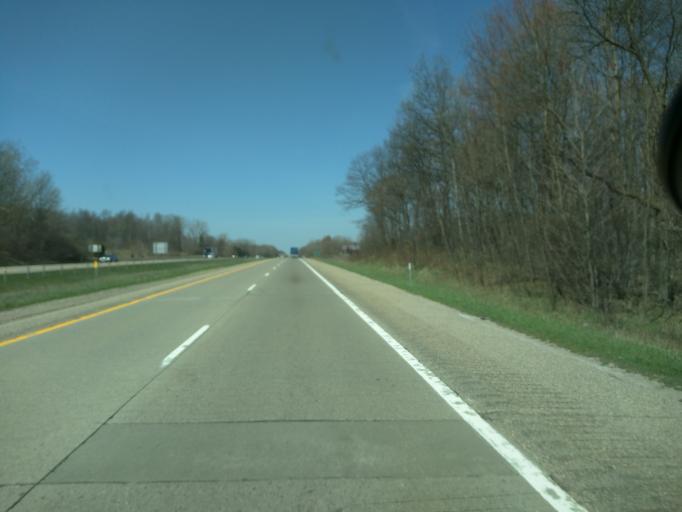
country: US
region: Michigan
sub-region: Kent County
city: Lowell
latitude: 42.8788
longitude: -85.3845
